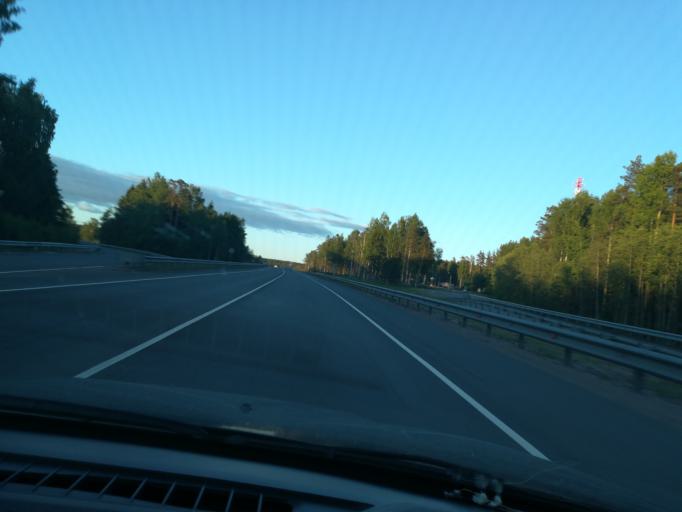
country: RU
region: Leningrad
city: Yakovlevo
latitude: 60.3605
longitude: 29.5237
